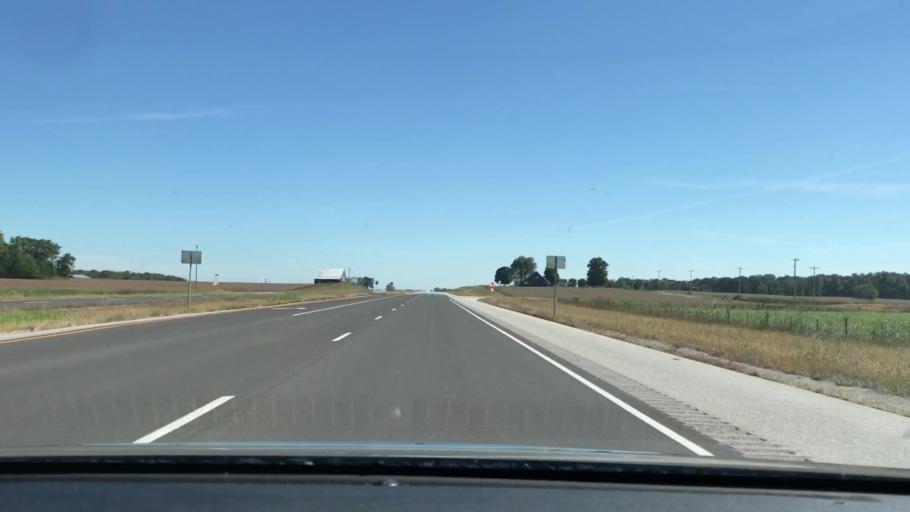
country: US
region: Kentucky
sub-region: Todd County
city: Elkton
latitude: 36.8065
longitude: -87.0512
